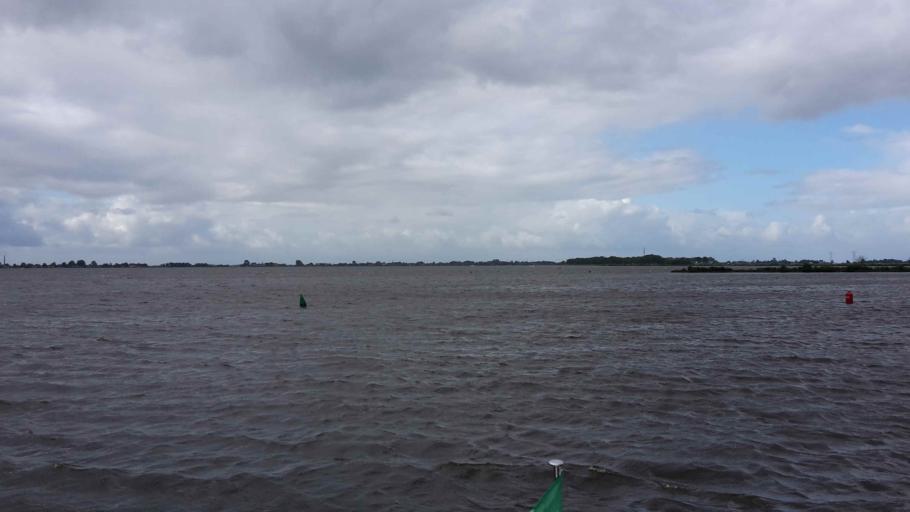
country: NL
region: Friesland
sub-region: Gemeente Skarsterlan
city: Sint Nicolaasga
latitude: 52.9000
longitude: 5.7784
